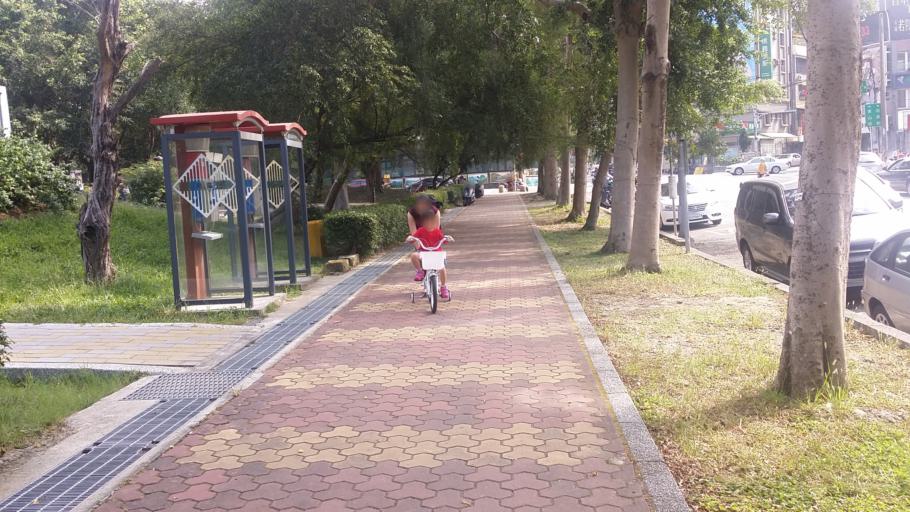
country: TW
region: Taiwan
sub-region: Hsinchu
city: Hsinchu
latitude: 24.7989
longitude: 120.9778
